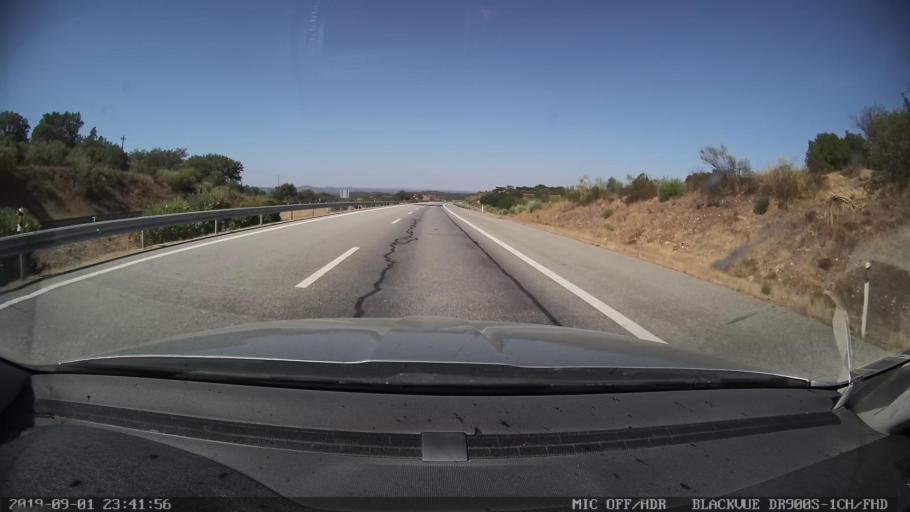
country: PT
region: Evora
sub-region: Estremoz
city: Estremoz
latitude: 38.8089
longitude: -7.5342
